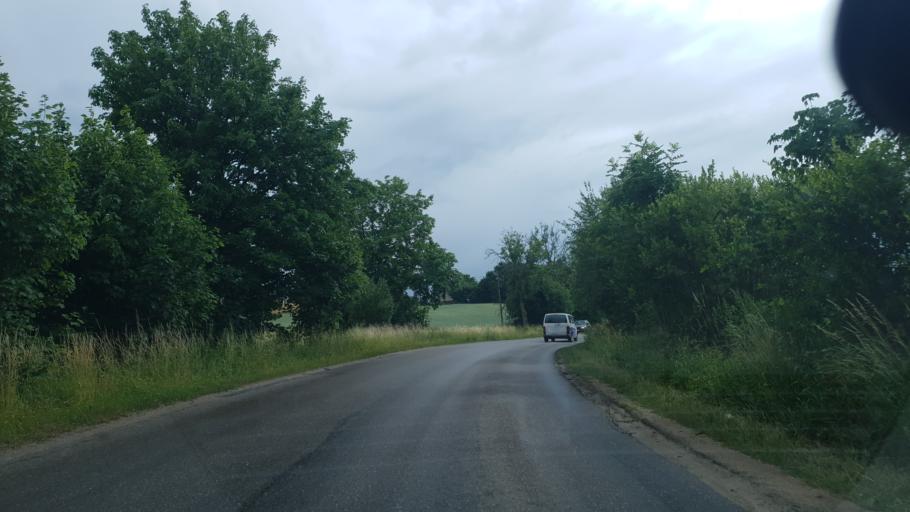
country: PL
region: Pomeranian Voivodeship
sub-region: Powiat kartuski
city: Przodkowo
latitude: 54.3590
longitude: 18.2429
